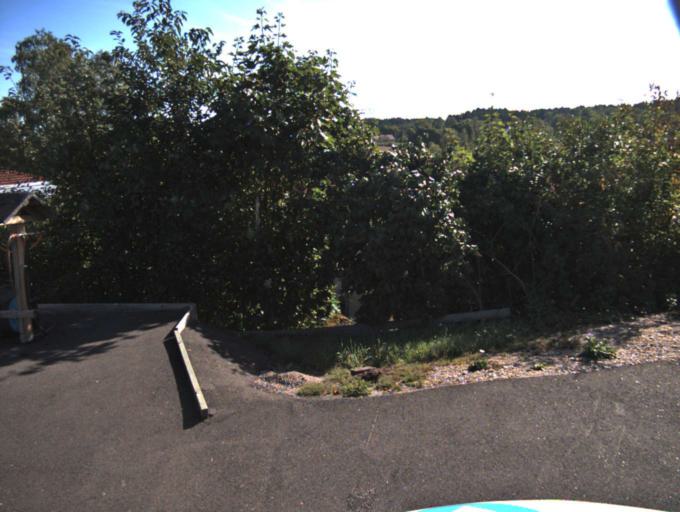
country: SE
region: Vaestra Goetaland
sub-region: Ulricehamns Kommun
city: Ulricehamn
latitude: 57.8999
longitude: 13.4713
